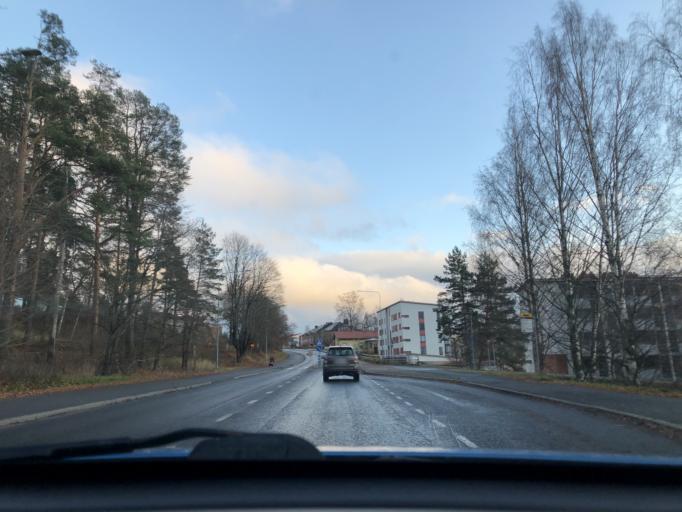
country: FI
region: Pirkanmaa
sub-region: Tampere
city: Kangasala
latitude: 61.4647
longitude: 24.0581
